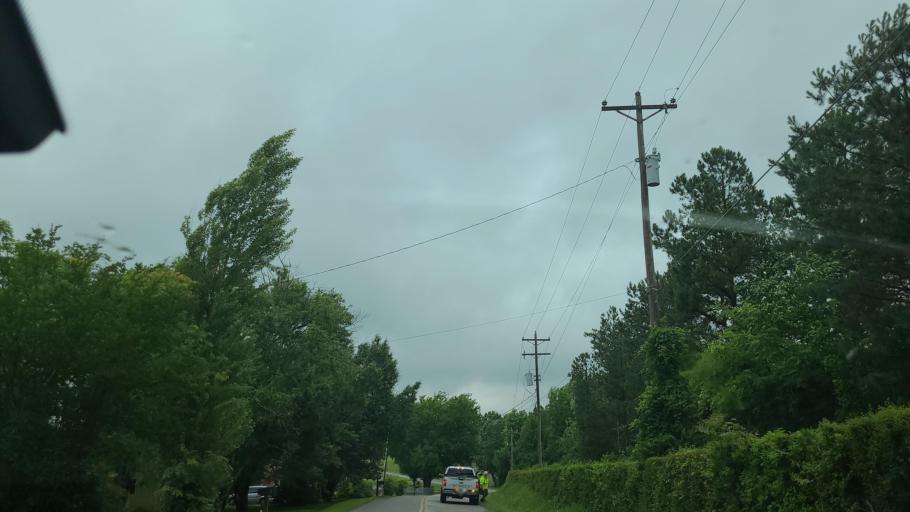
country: US
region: Tennessee
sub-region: Rhea County
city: Dayton
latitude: 35.5060
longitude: -84.9873
